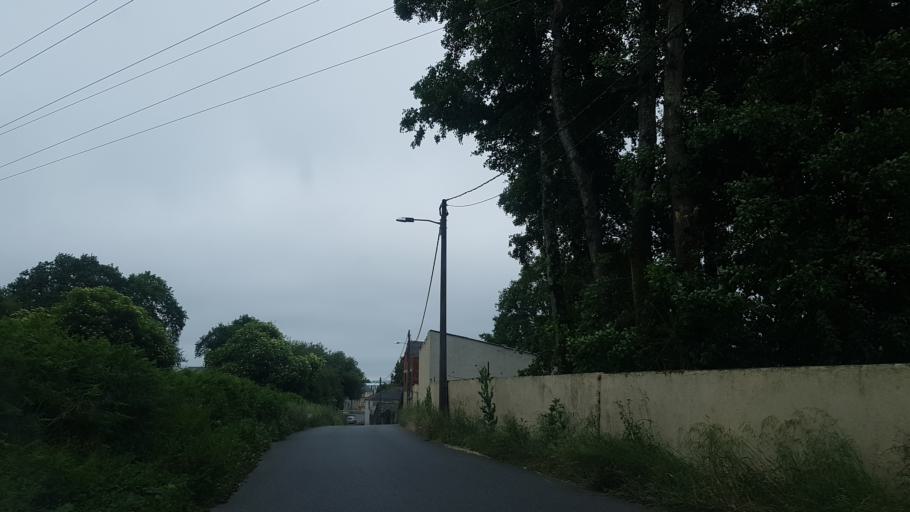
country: ES
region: Galicia
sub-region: Provincia de Lugo
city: Lugo
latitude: 43.0436
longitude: -7.5805
